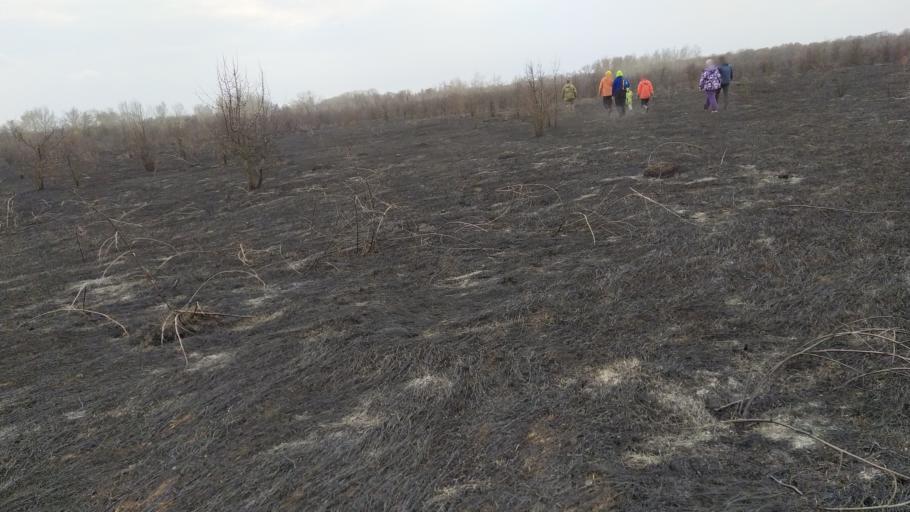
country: RU
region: Rostov
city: Semikarakorsk
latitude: 47.5441
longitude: 40.6842
